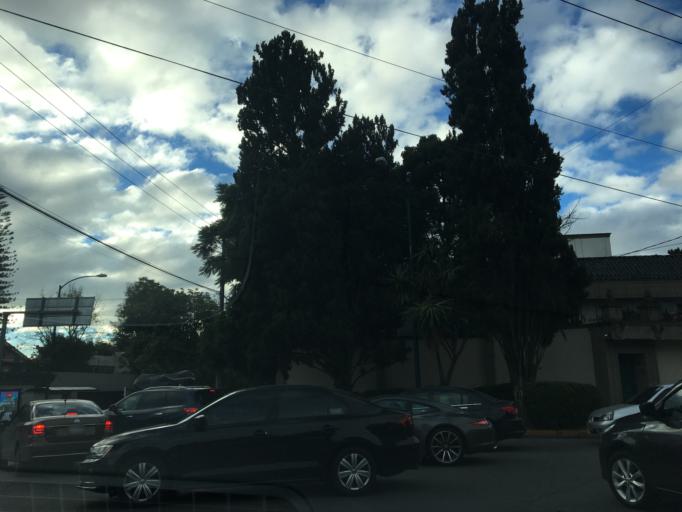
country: MX
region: Mexico City
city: Polanco
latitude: 19.4206
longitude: -99.2081
